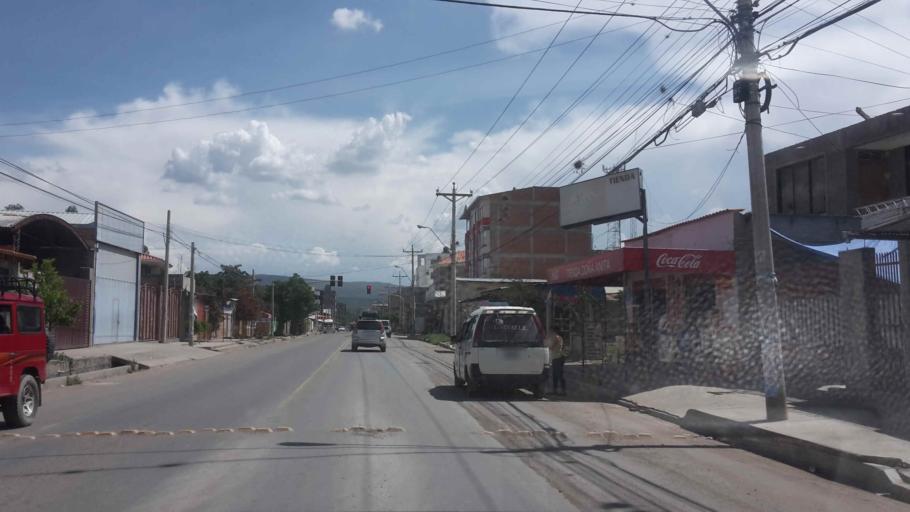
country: BO
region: Cochabamba
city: Cochabamba
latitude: -17.3838
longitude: -66.2364
